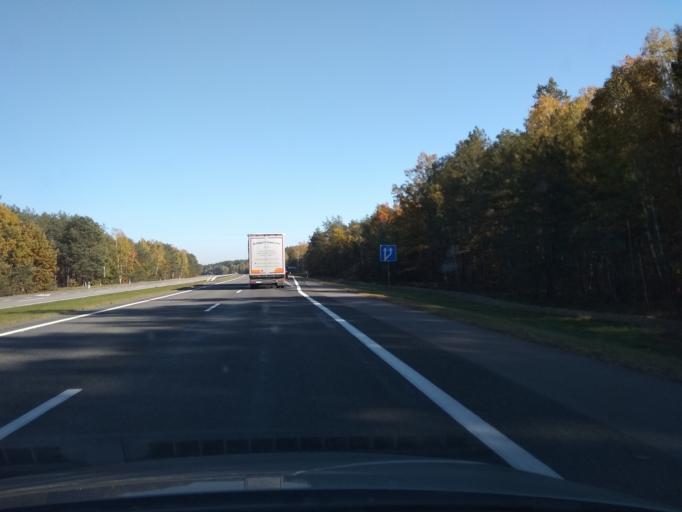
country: BY
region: Brest
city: Antopal'
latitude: 52.3646
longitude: 24.7304
